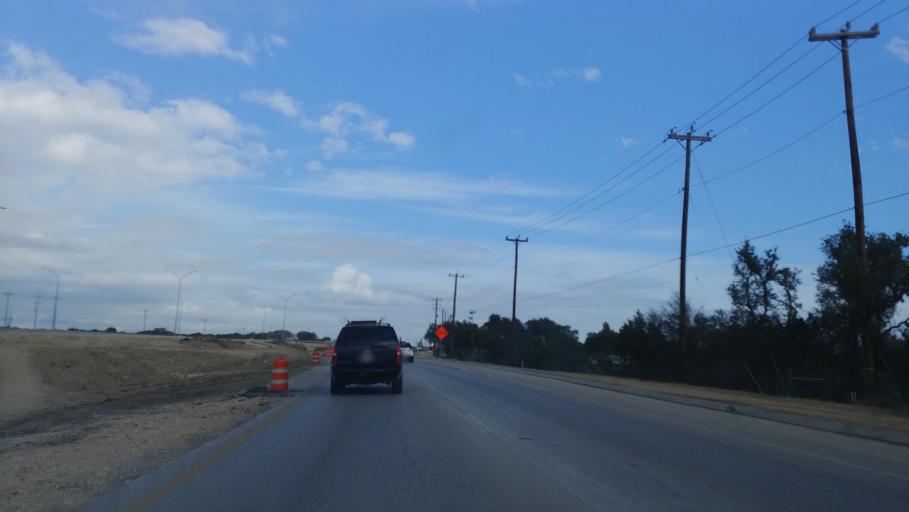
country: US
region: Texas
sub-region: Bexar County
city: Leon Valley
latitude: 29.4503
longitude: -98.7110
